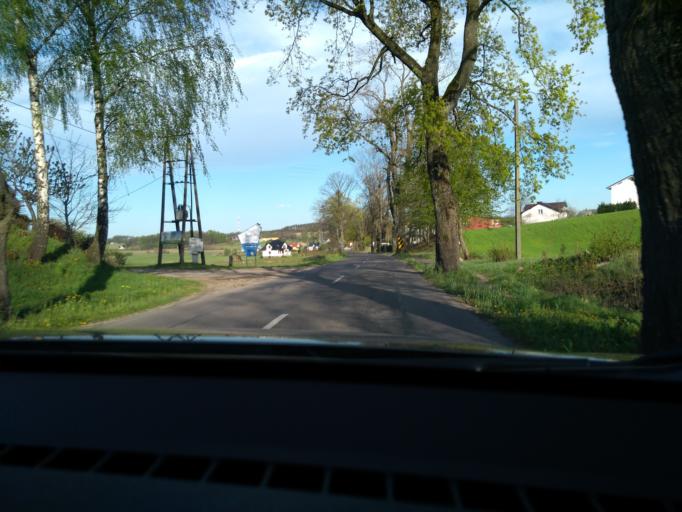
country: PL
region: Pomeranian Voivodeship
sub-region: Powiat kartuski
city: Suleczyno
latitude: 54.3277
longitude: 17.7819
